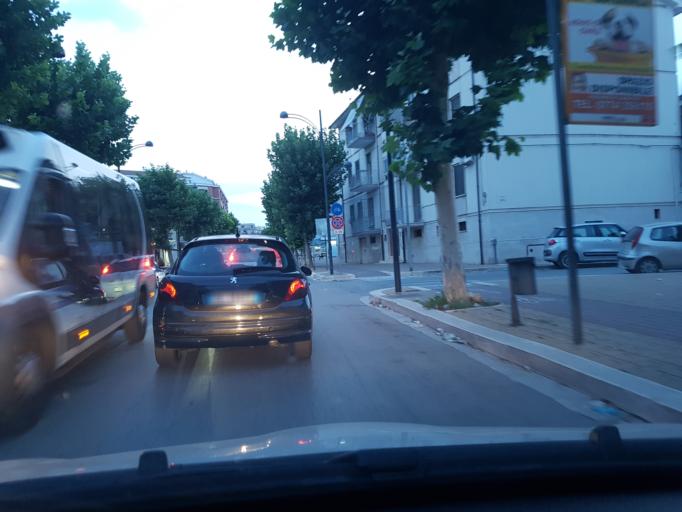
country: IT
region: Apulia
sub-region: Provincia di Foggia
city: Cerignola
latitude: 41.2604
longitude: 15.9017
